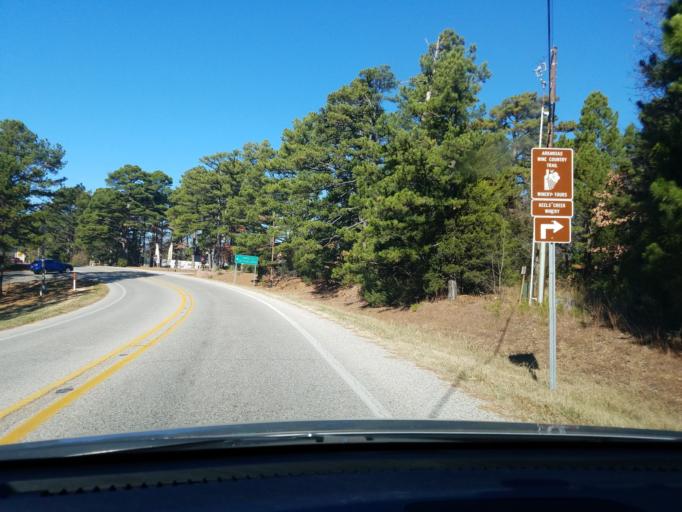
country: US
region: Arkansas
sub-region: Carroll County
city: Eureka Springs
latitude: 36.3893
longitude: -93.7125
